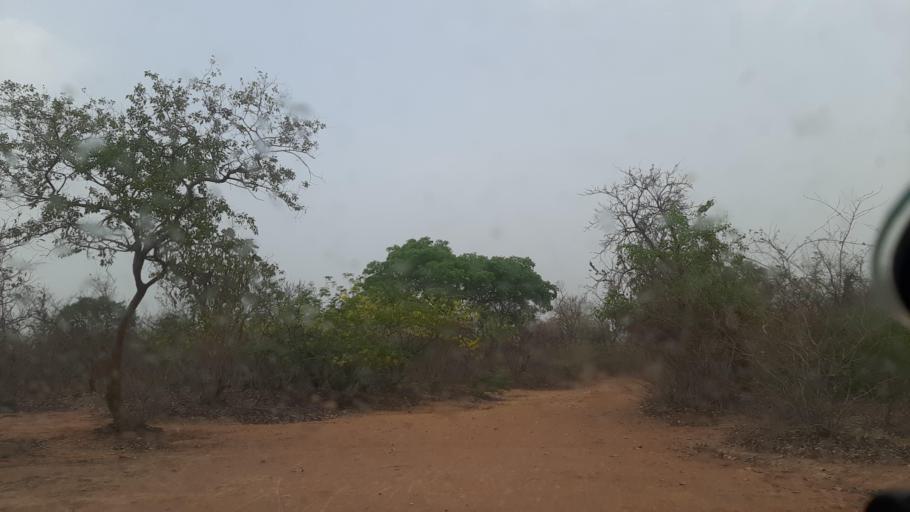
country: BF
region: Boucle du Mouhoun
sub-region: Province des Banwa
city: Salanso
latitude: 11.8627
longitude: -4.4378
